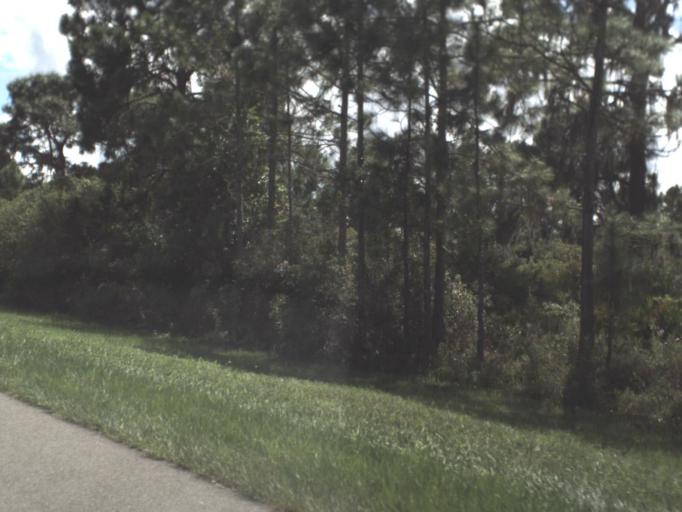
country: US
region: Florida
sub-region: Sarasota County
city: The Meadows
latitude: 27.4133
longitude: -82.3458
